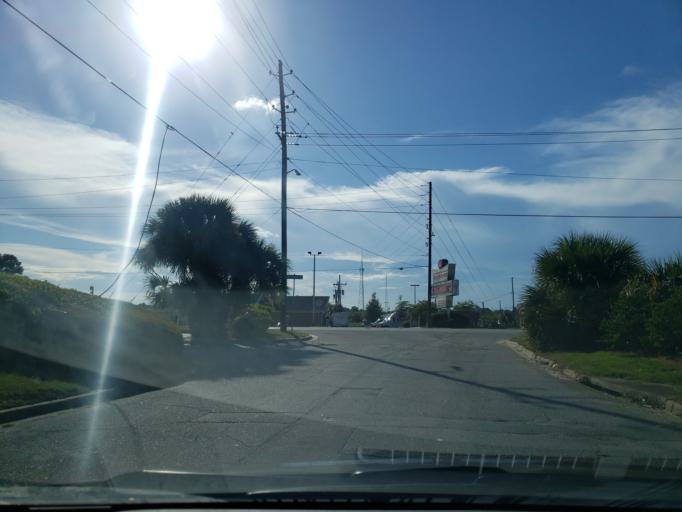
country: US
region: Georgia
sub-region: Chatham County
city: Thunderbolt
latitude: 32.0399
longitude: -81.0644
